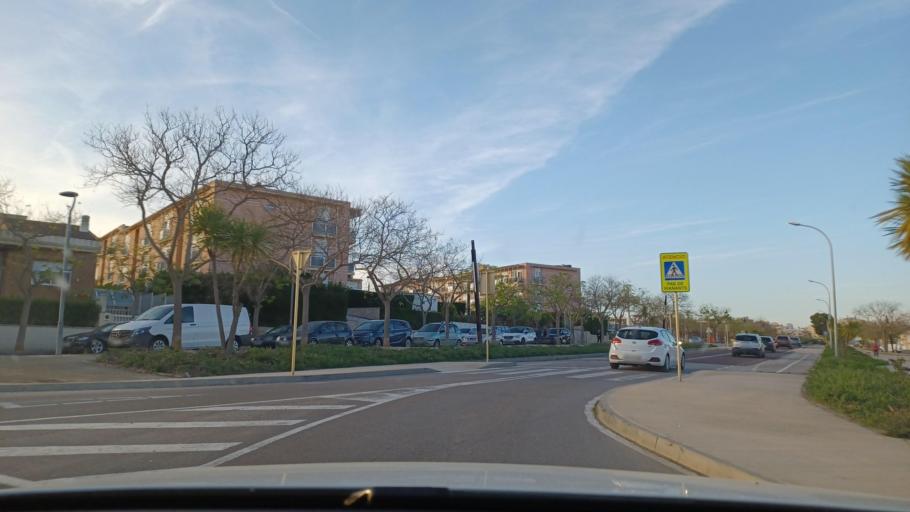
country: ES
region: Catalonia
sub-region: Provincia de Tarragona
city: Sant Carles de la Rapita
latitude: 40.6080
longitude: 0.5834
